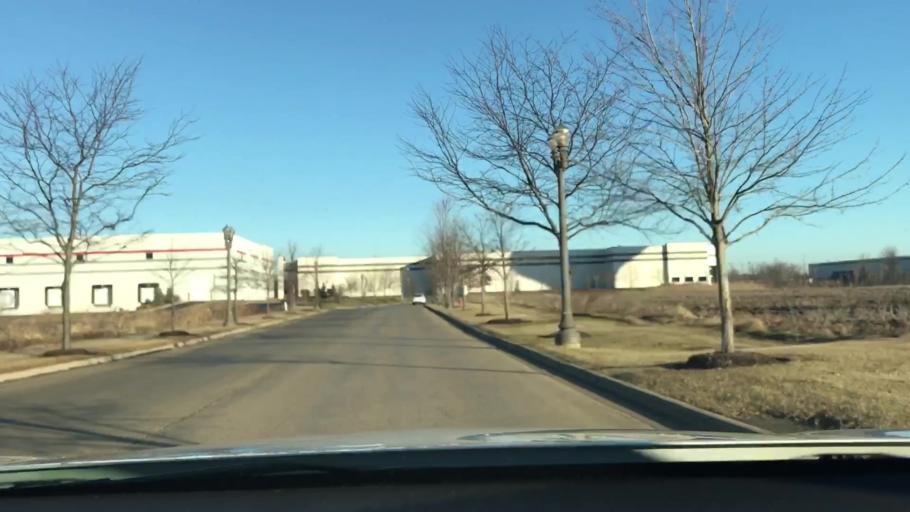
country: US
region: Illinois
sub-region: Kane County
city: Gilberts
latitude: 42.0735
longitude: -88.3468
